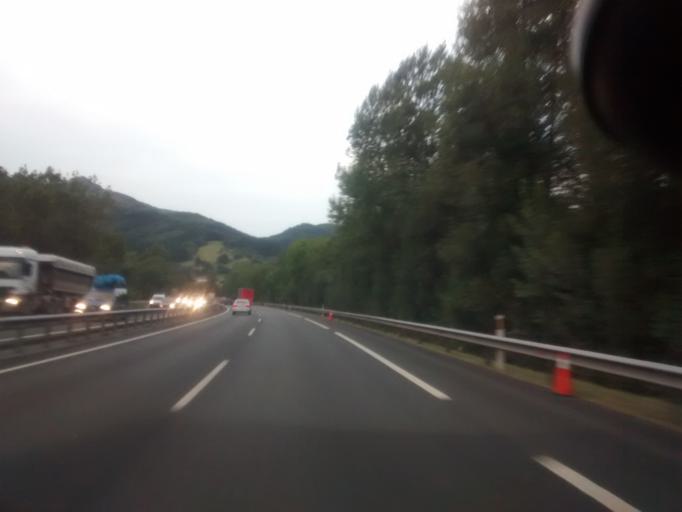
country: ES
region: Basque Country
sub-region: Provincia de Guipuzcoa
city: Cestona
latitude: 43.2627
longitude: -2.2784
